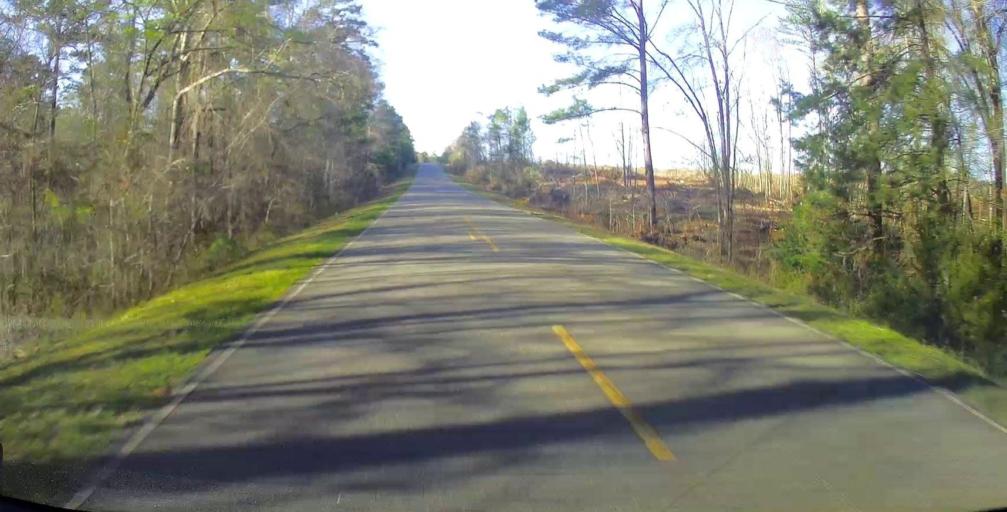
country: US
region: Georgia
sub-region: Pulaski County
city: Hawkinsville
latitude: 32.2848
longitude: -83.5907
